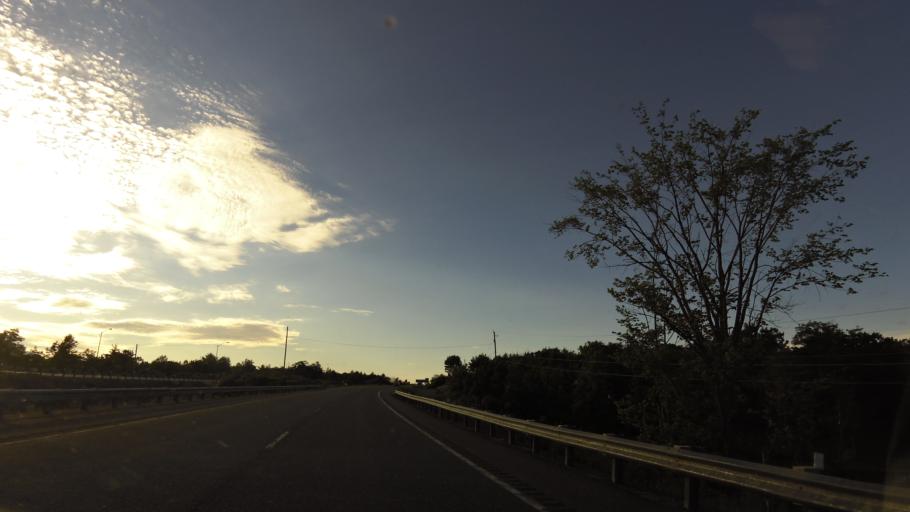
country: CA
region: Ontario
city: Midland
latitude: 44.9002
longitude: -79.7680
